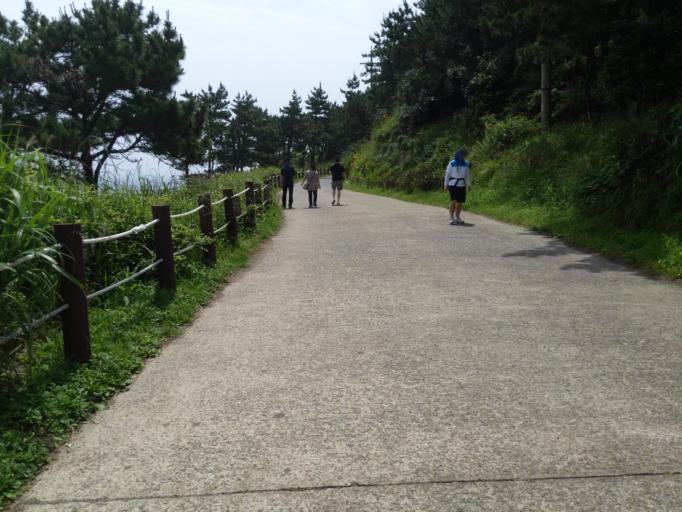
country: KR
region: Jeju-do
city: Gaigeturi
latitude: 33.2032
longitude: 126.2908
